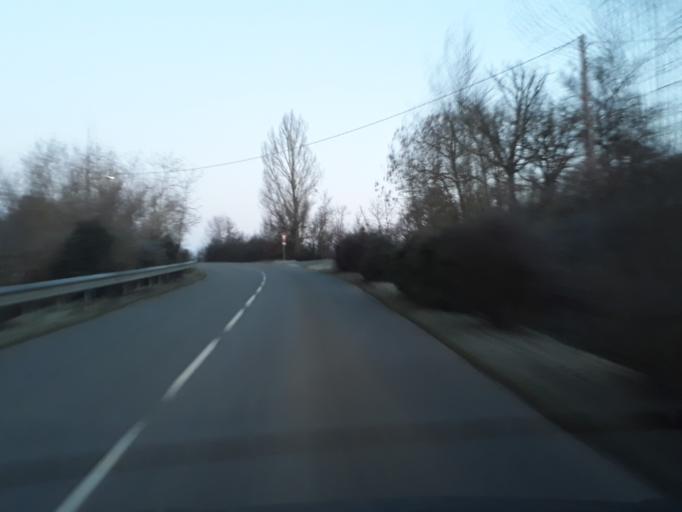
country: FR
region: Midi-Pyrenees
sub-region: Departement du Gers
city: Samatan
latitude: 43.4929
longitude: 0.9263
